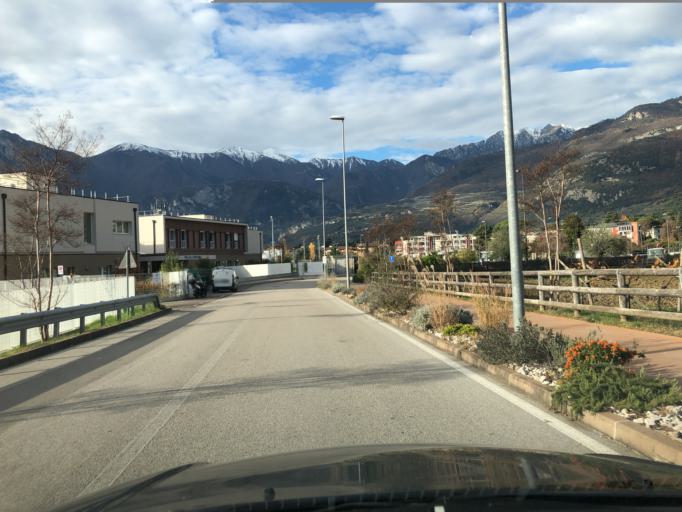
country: IT
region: Trentino-Alto Adige
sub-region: Provincia di Trento
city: Arco
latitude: 45.9159
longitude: 10.8916
